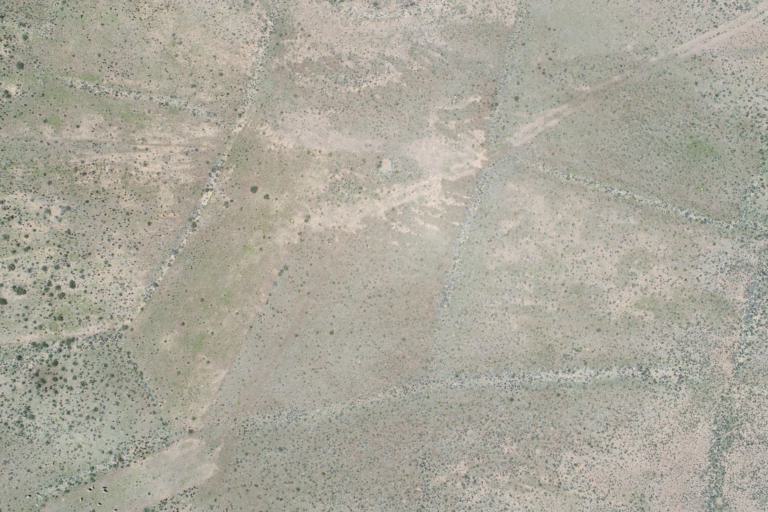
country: BO
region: La Paz
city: Curahuara de Carangas
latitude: -17.3085
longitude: -68.5040
